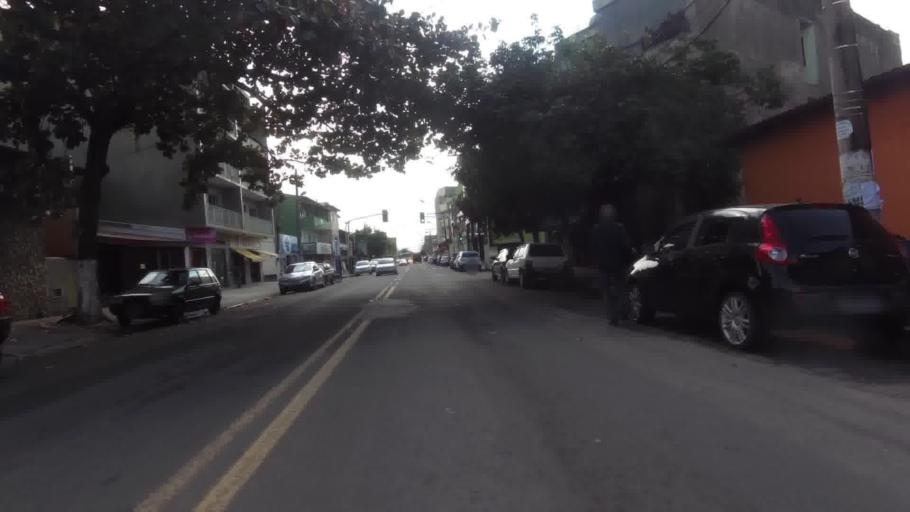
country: BR
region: Espirito Santo
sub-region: Marataizes
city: Marataizes
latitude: -21.0394
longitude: -40.8216
